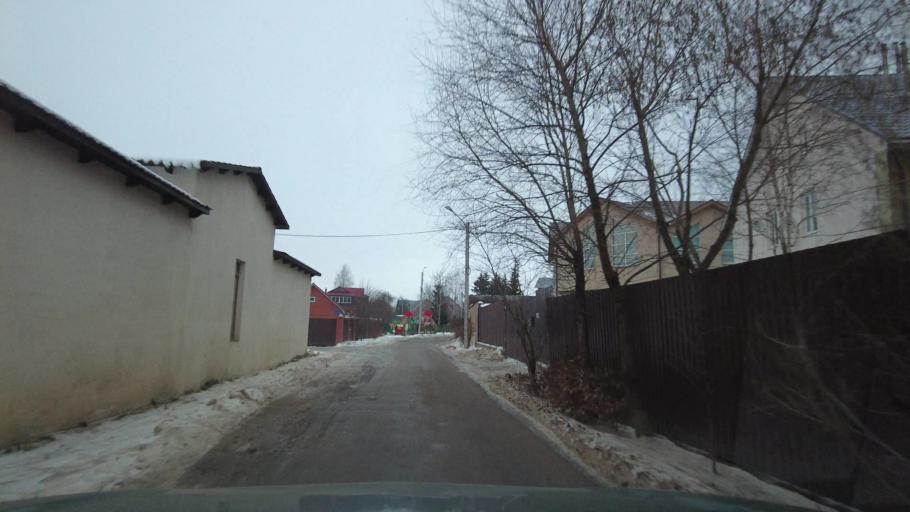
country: RU
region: Moskovskaya
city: Novopodrezkovo
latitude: 55.9784
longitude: 37.3852
